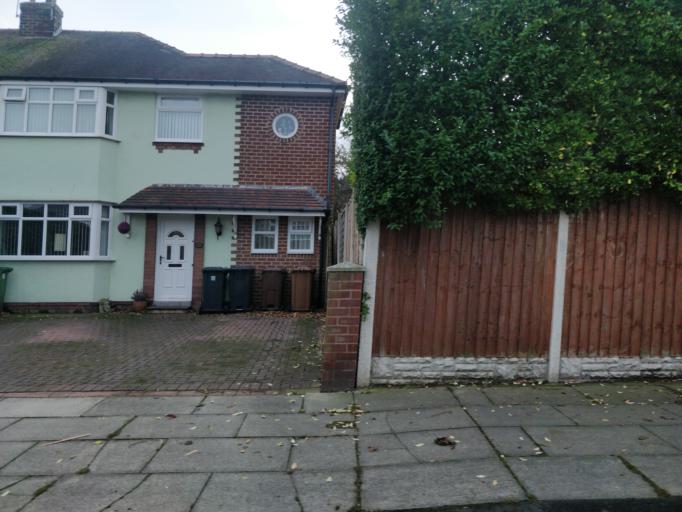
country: GB
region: England
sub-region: Lancashire
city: Banks
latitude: 53.6694
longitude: -2.9554
